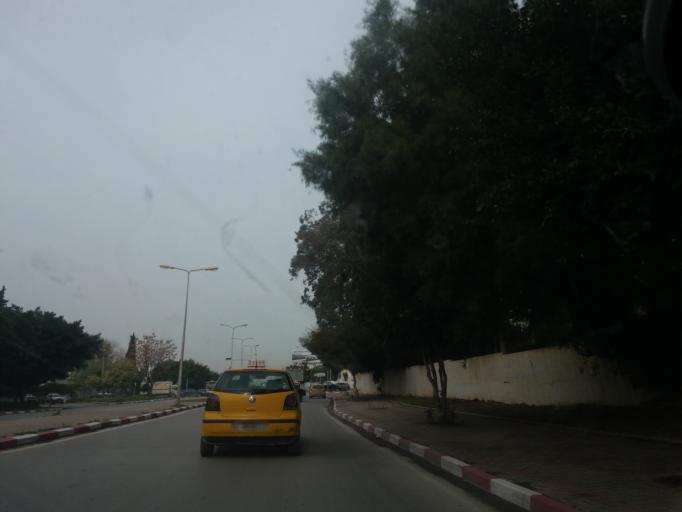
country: TN
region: Tunis
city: Tunis
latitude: 36.8465
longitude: 10.1610
